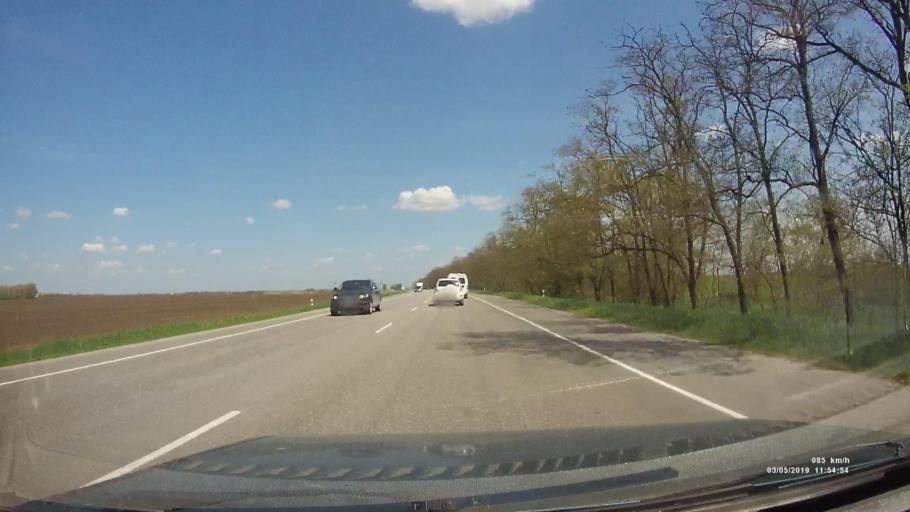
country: RU
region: Rostov
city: Bagayevskaya
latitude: 47.1747
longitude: 40.2859
